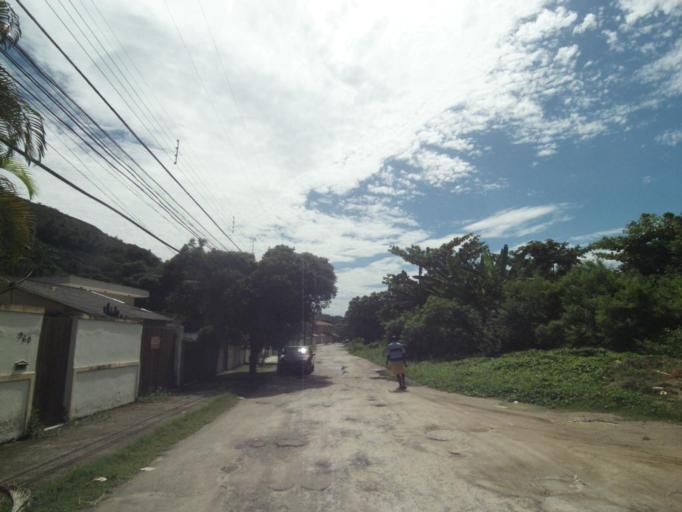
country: BR
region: Rio de Janeiro
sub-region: Niteroi
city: Niteroi
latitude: -22.9487
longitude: -43.0450
